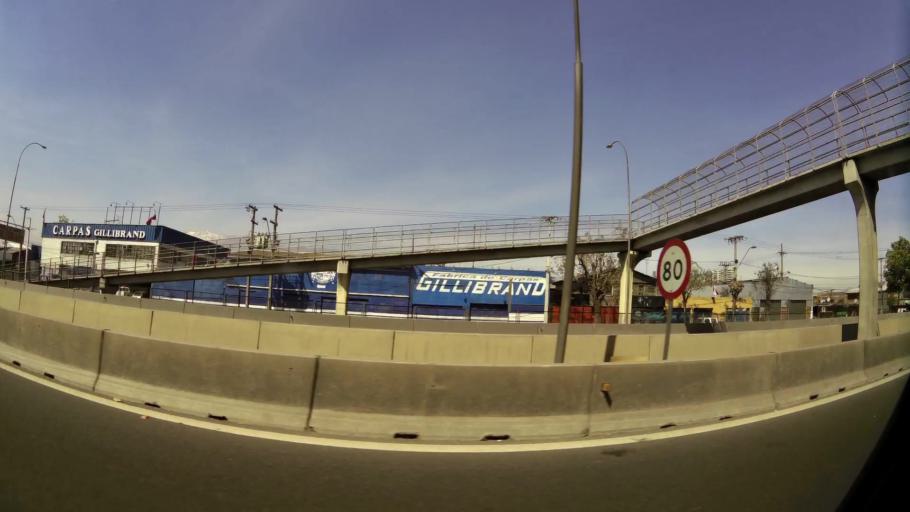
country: CL
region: Santiago Metropolitan
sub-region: Provincia de Santiago
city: Santiago
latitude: -33.5045
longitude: -70.6682
